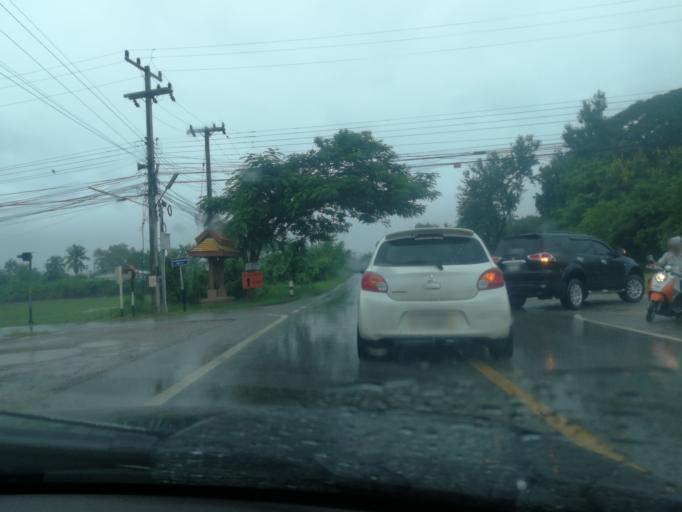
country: TH
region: Chiang Mai
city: San Pa Tong
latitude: 18.6290
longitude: 98.8992
